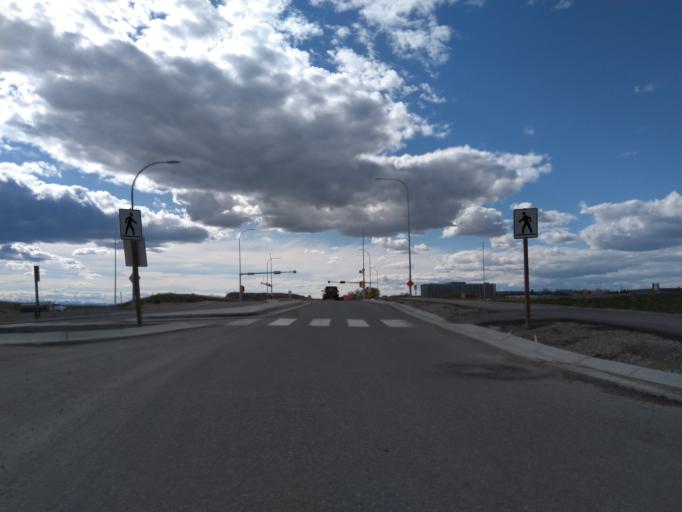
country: CA
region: Alberta
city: Calgary
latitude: 51.0031
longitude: -114.1416
